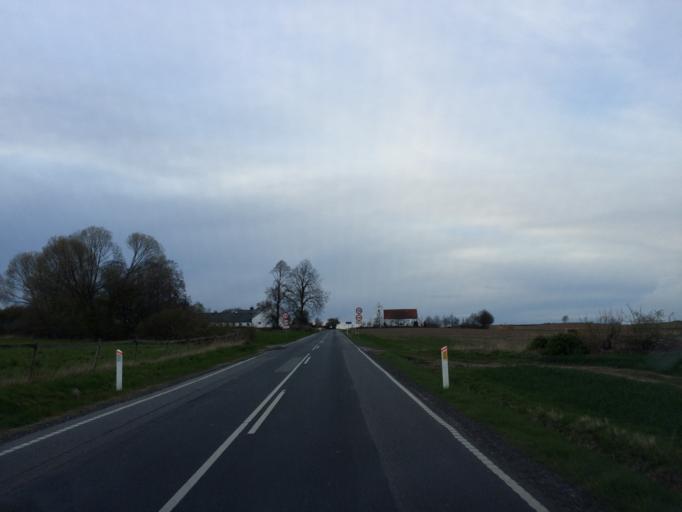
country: DK
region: South Denmark
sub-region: Odense Kommune
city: Bellinge
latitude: 55.3477
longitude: 10.2778
